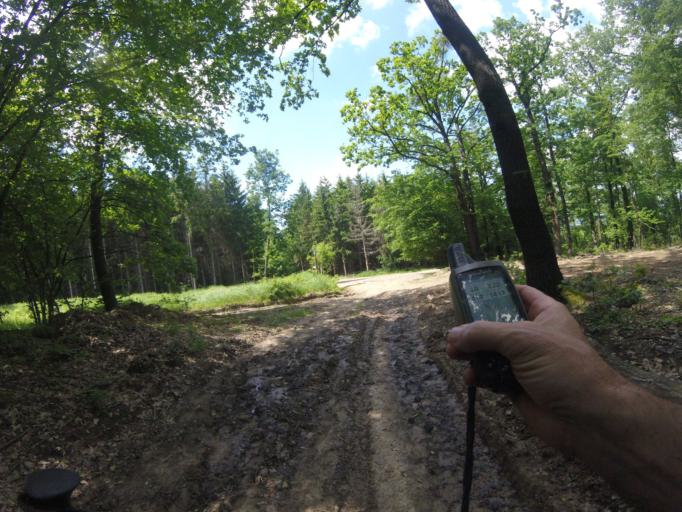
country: HU
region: Nograd
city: Matraverebely
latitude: 47.9398
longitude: 19.8078
